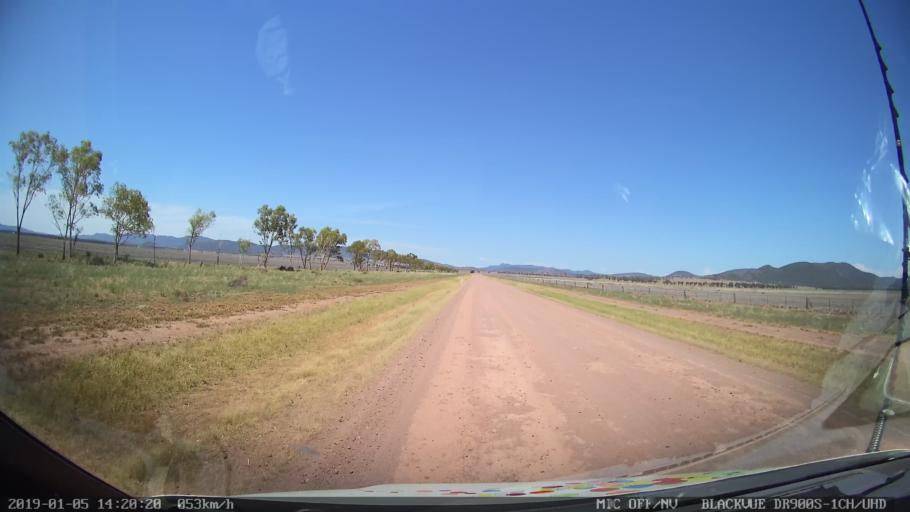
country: AU
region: New South Wales
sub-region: Liverpool Plains
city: Quirindi
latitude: -31.2490
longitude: 150.5038
